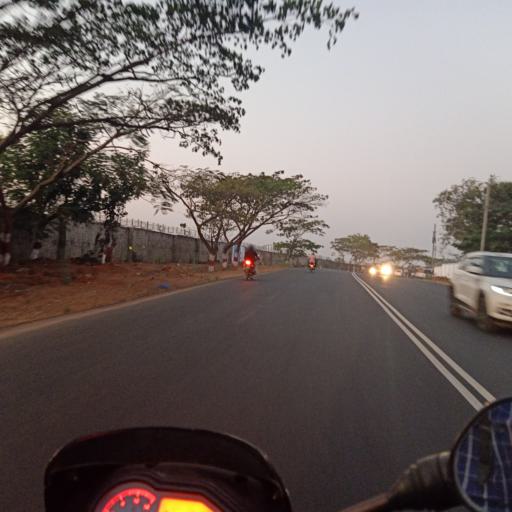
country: IN
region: Telangana
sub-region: Rangareddi
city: Secunderabad
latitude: 17.5533
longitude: 78.5363
